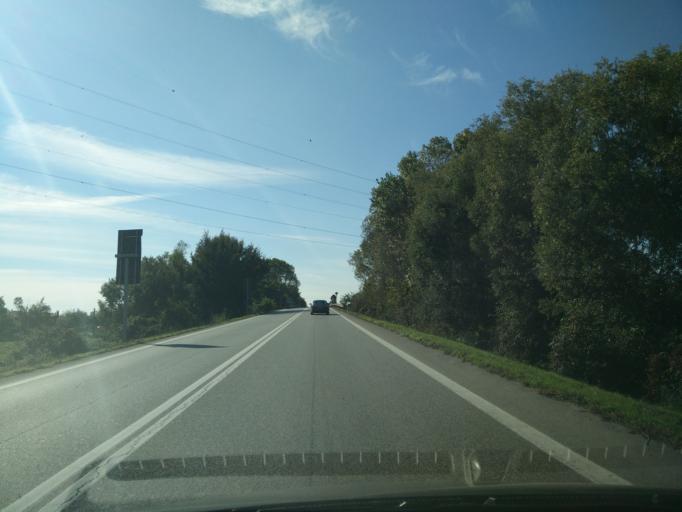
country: IT
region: Veneto
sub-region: Provincia di Venezia
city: Mestre
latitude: 45.4406
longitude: 12.2013
